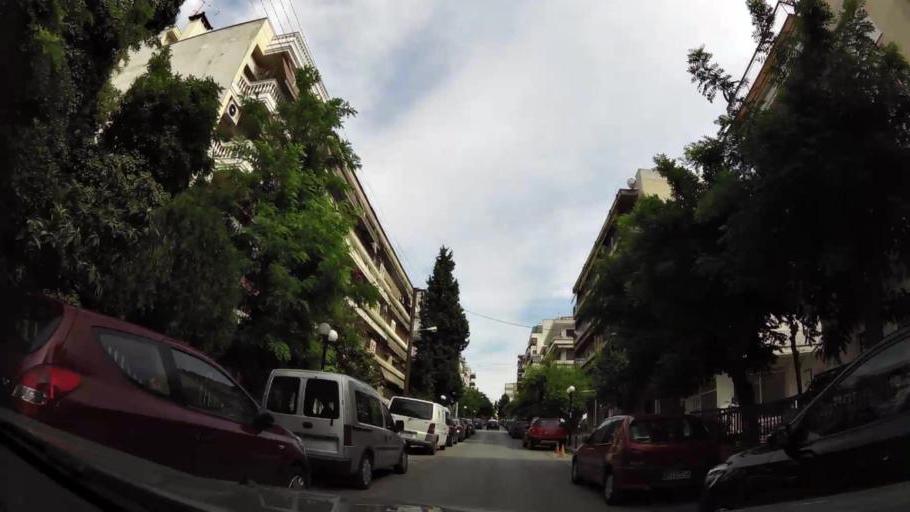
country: GR
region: Central Macedonia
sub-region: Nomos Thessalonikis
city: Kalamaria
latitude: 40.5859
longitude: 22.9502
